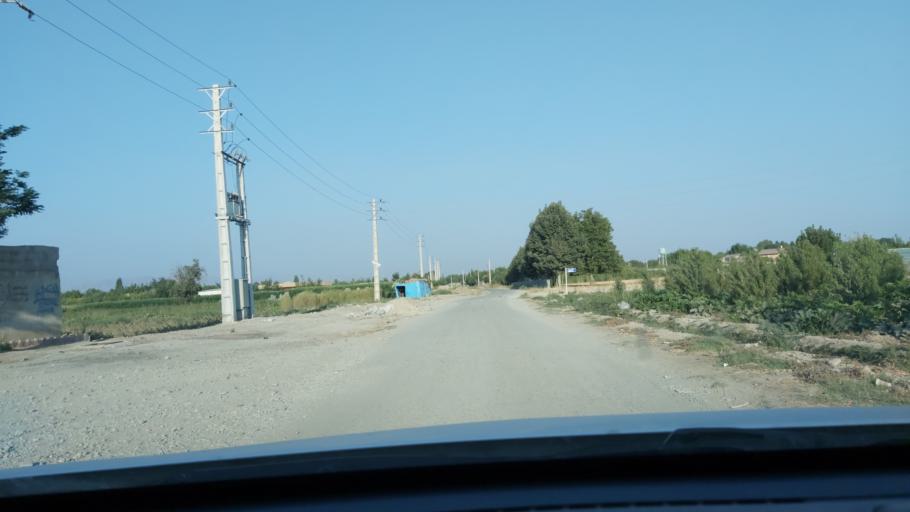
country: IR
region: Alborz
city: Hashtgerd
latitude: 35.8589
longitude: 50.6953
